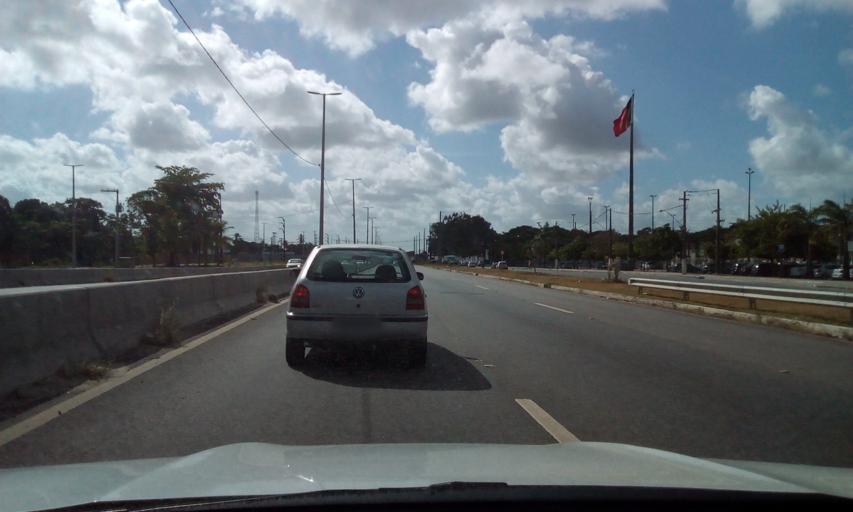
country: BR
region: Paraiba
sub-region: Joao Pessoa
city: Joao Pessoa
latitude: -7.1695
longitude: -34.8771
